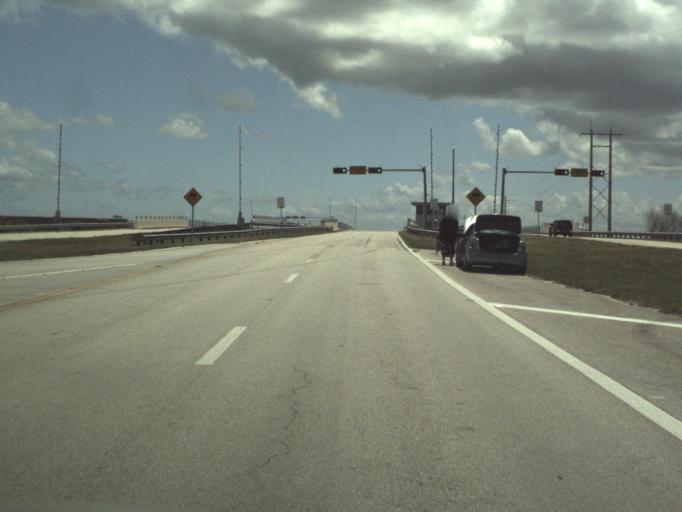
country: US
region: Florida
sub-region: Brevard County
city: Cape Canaveral
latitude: 28.4107
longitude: -80.6323
